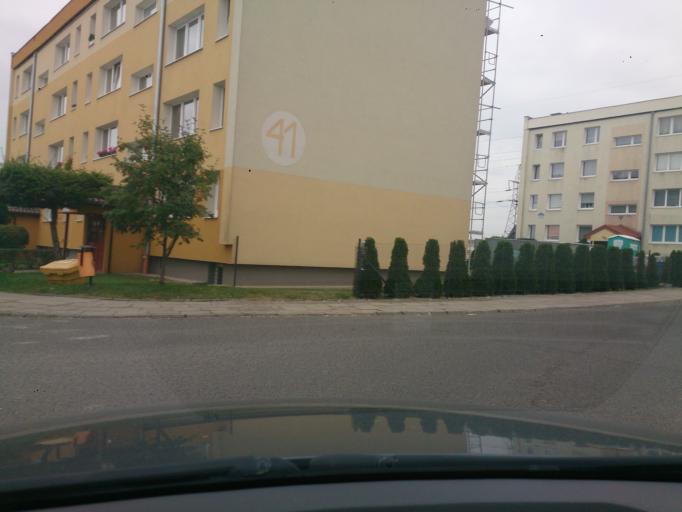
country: PL
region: Pomeranian Voivodeship
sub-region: Powiat wejherowski
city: Reda
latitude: 54.6013
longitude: 18.3571
